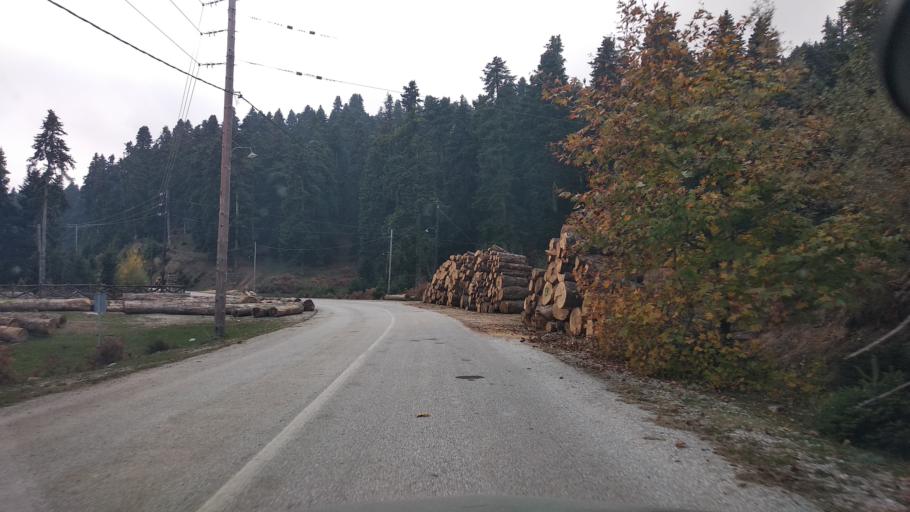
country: GR
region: Thessaly
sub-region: Trikala
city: Fiki
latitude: 39.5795
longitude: 21.4920
